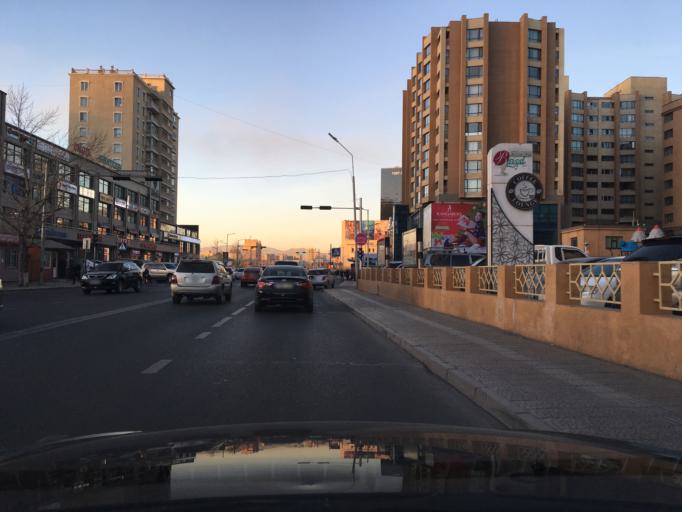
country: MN
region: Ulaanbaatar
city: Ulaanbaatar
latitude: 47.8947
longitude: 106.9087
